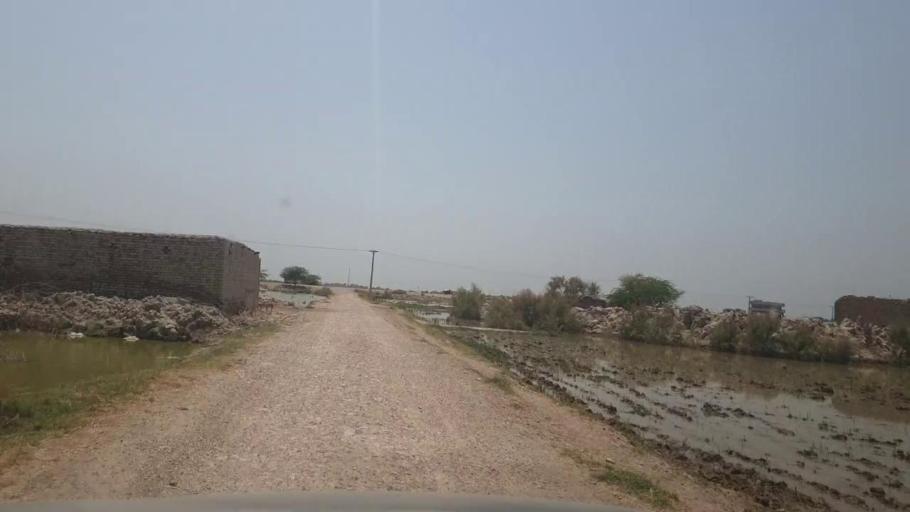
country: PK
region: Sindh
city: Lakhi
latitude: 27.8408
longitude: 68.6619
